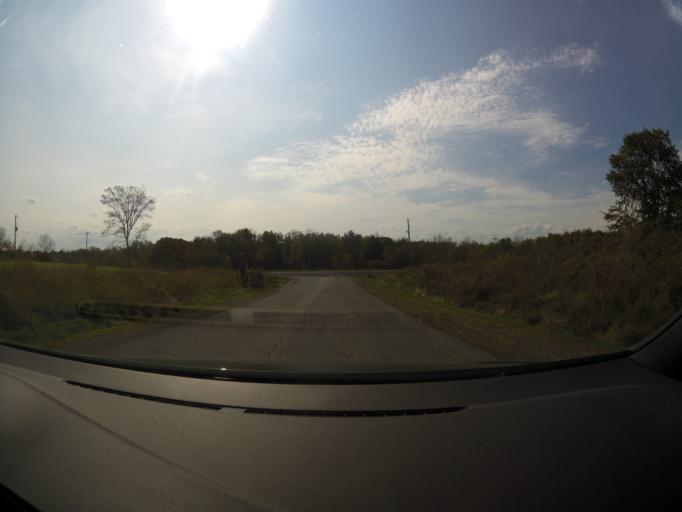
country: CA
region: Ontario
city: Bells Corners
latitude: 45.4401
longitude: -75.9949
